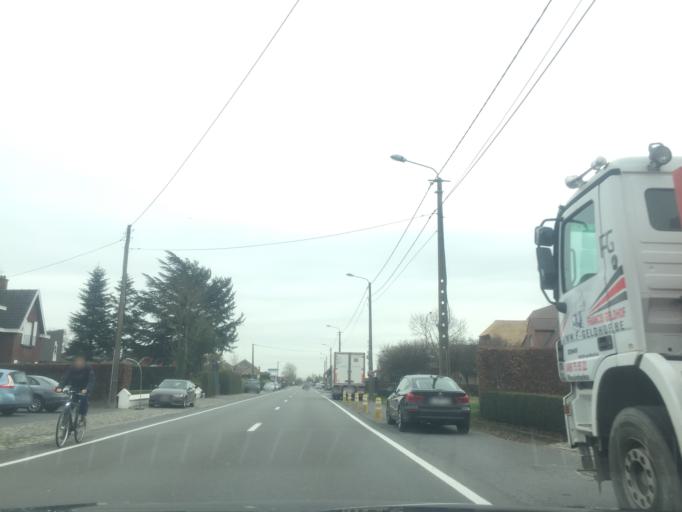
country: BE
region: Flanders
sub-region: Provincie West-Vlaanderen
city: Oostrozebeke
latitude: 50.9202
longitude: 3.3435
